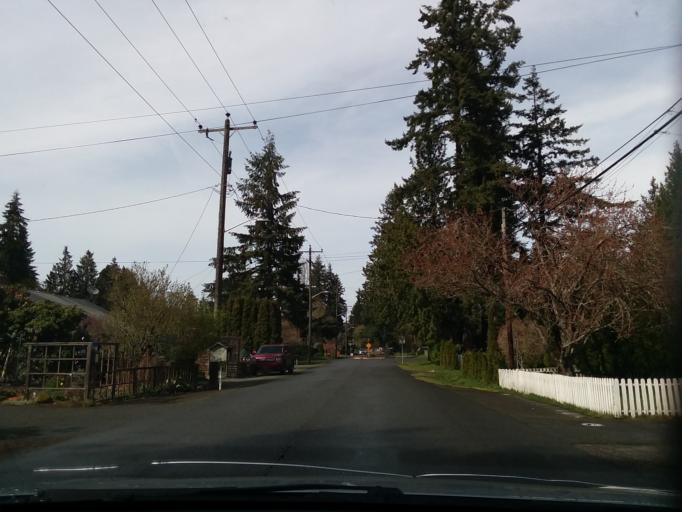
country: US
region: Washington
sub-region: King County
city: Shoreline
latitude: 47.7717
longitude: -122.3486
